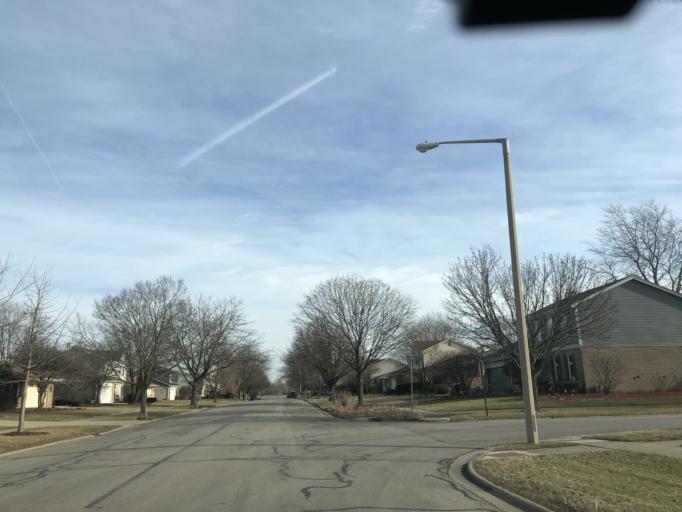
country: US
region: Illinois
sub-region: DuPage County
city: Woodridge
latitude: 41.7173
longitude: -88.0242
